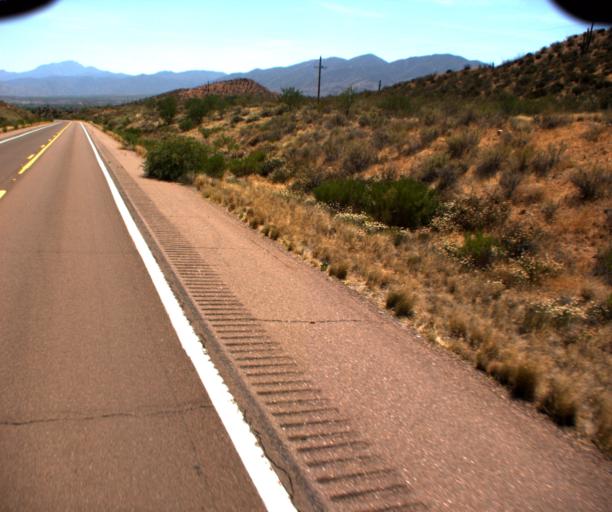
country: US
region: Arizona
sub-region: Gila County
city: Tonto Basin
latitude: 33.9026
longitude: -111.3105
